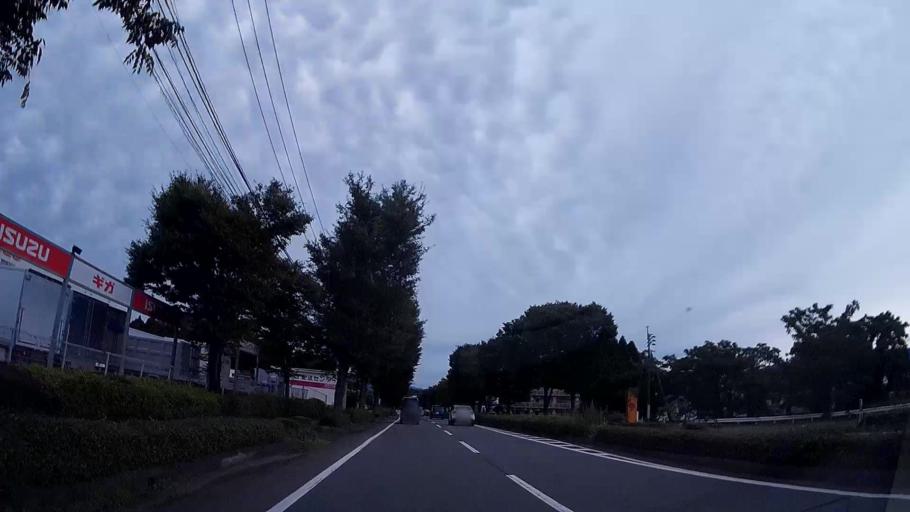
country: JP
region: Kumamoto
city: Ozu
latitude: 32.8892
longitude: 130.8543
